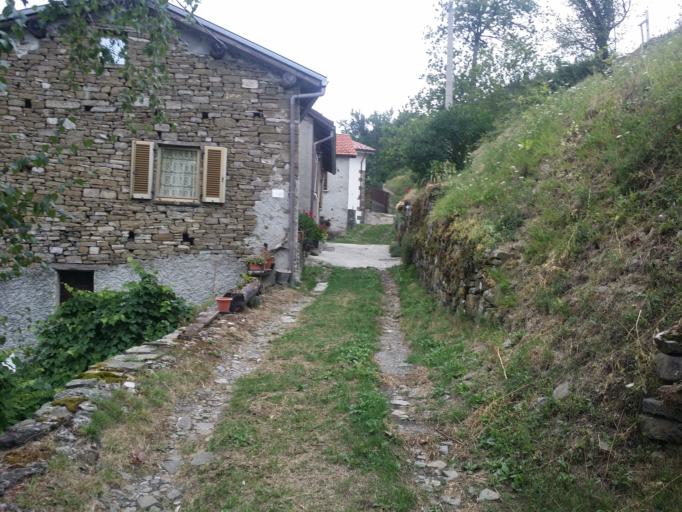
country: IT
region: Emilia-Romagna
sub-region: Provincia di Parma
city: Borgo Val di Taro
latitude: 44.5319
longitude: 9.7921
